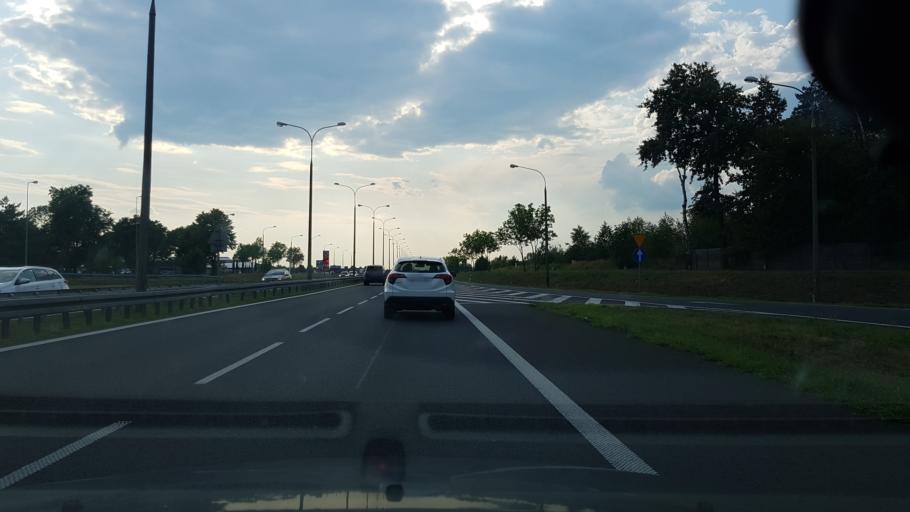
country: PL
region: Masovian Voivodeship
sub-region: Powiat nowodworski
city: Zakroczym
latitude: 52.4411
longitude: 20.6379
